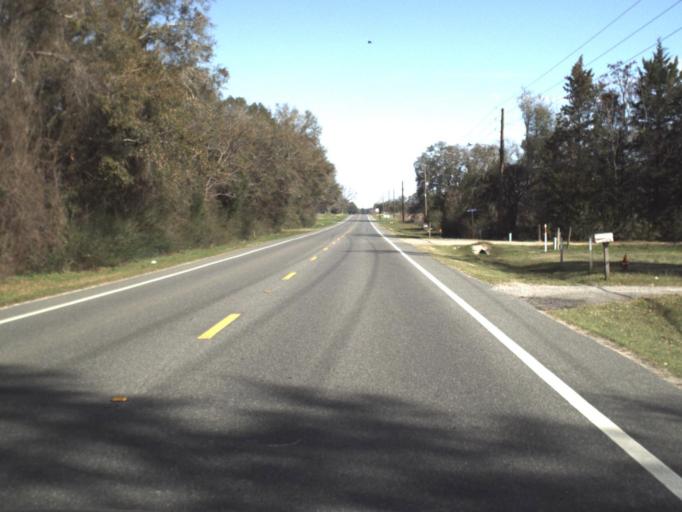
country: US
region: Florida
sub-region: Jackson County
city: Malone
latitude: 30.8965
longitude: -85.1611
